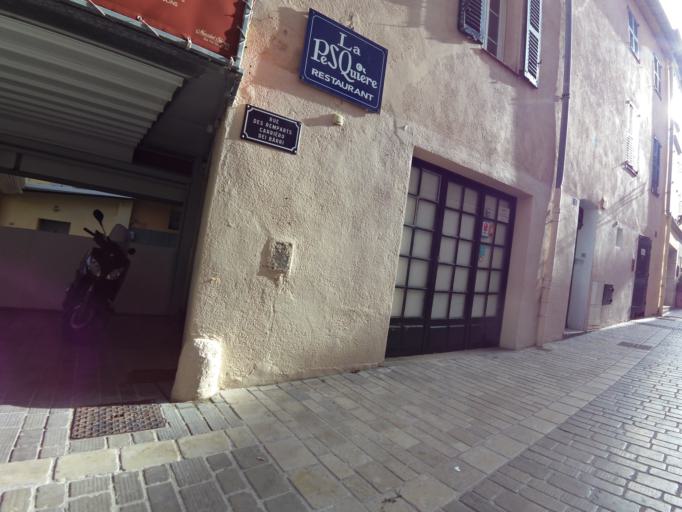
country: FR
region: Provence-Alpes-Cote d'Azur
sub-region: Departement du Var
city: Saint-Tropez
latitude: 43.2734
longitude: 6.6405
